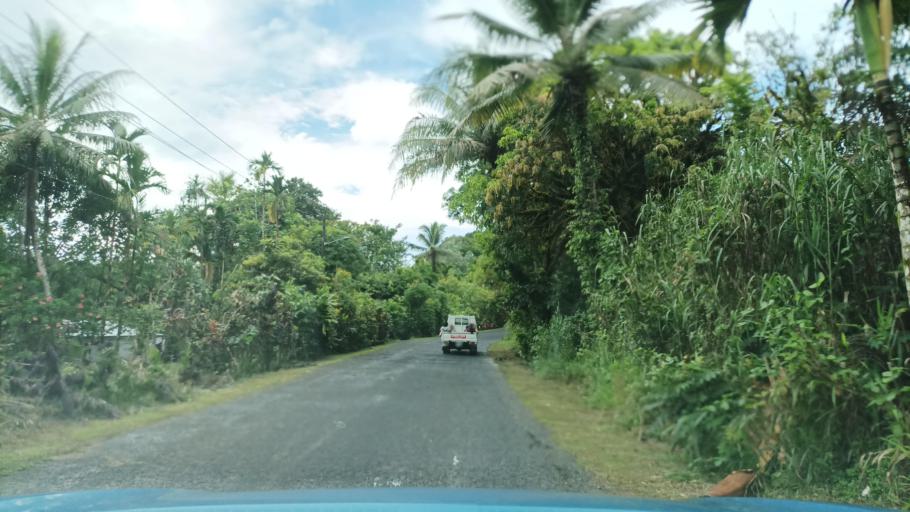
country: FM
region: Pohnpei
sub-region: Sokehs Municipality
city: Palikir - National Government Center
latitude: 6.8533
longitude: 158.1621
